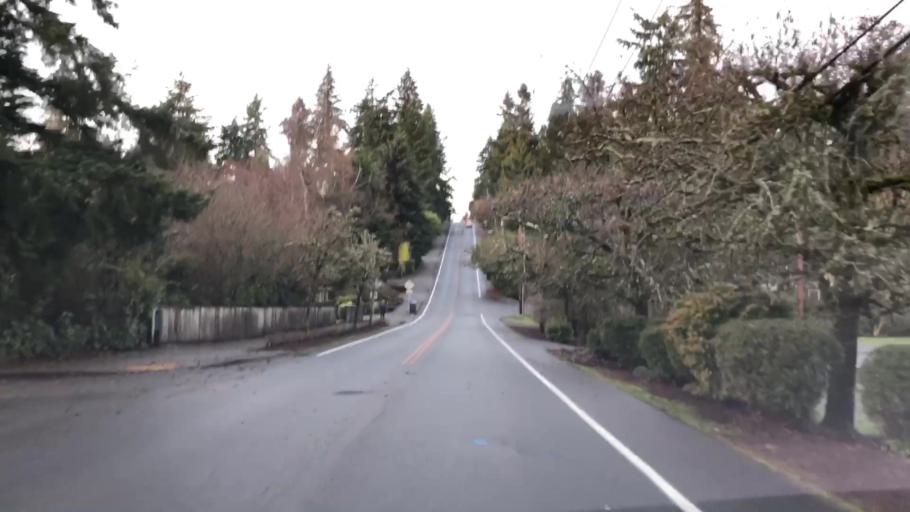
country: US
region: Washington
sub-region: King County
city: Eastgate
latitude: 47.5891
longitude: -122.1283
